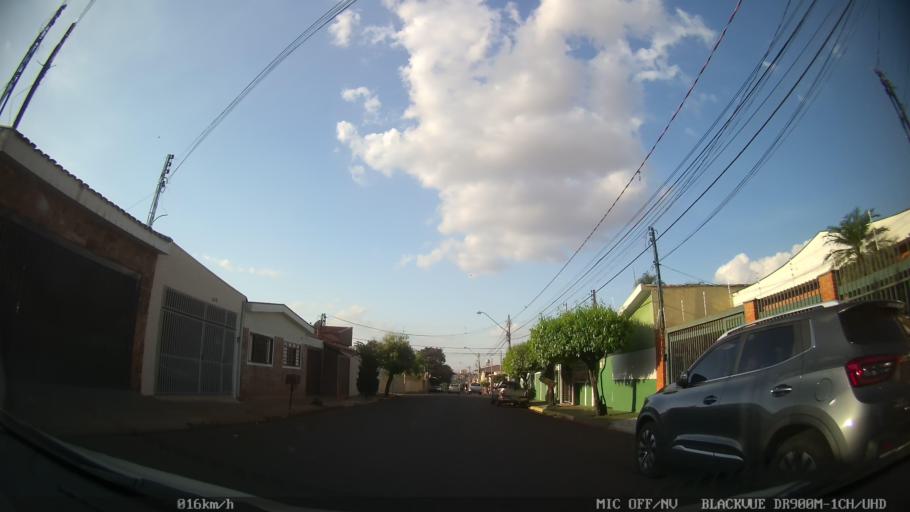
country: BR
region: Sao Paulo
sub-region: Ribeirao Preto
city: Ribeirao Preto
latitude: -21.1709
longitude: -47.8333
